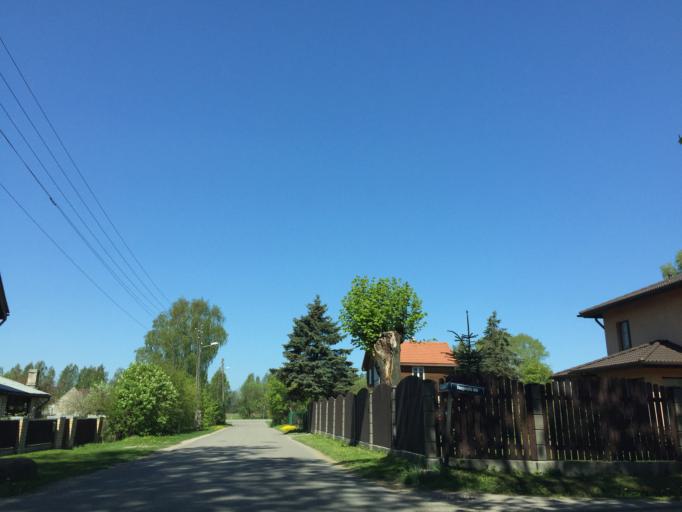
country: LV
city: Tireli
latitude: 56.9417
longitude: 23.6082
